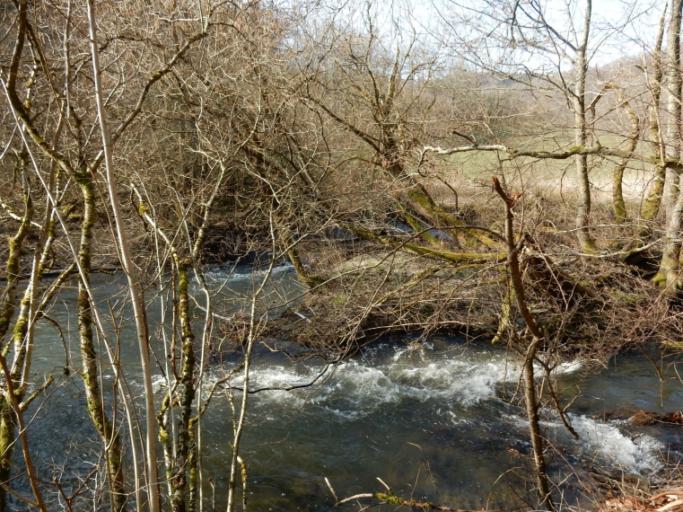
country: LU
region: Diekirch
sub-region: Canton de Wiltz
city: Winseler
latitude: 49.9728
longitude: 5.8830
